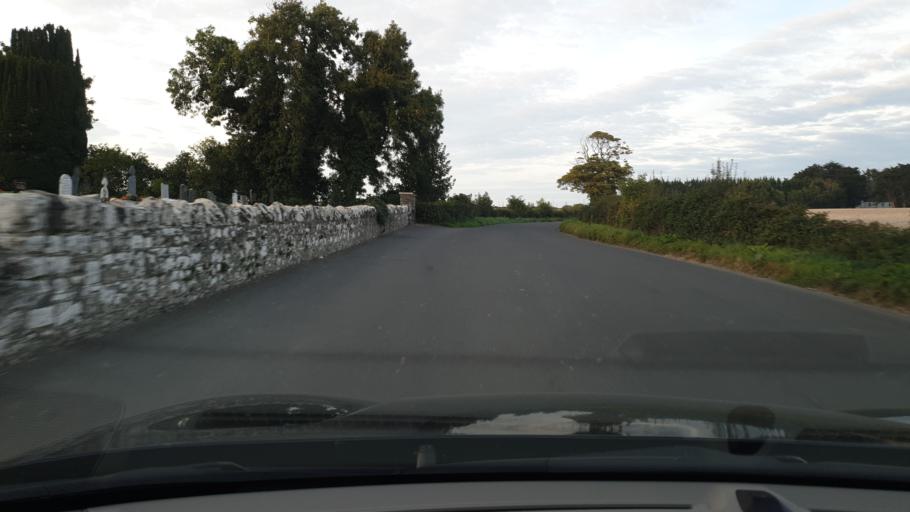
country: IE
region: Leinster
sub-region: An Mhi
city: Ashbourne
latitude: 53.5462
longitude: -6.3299
